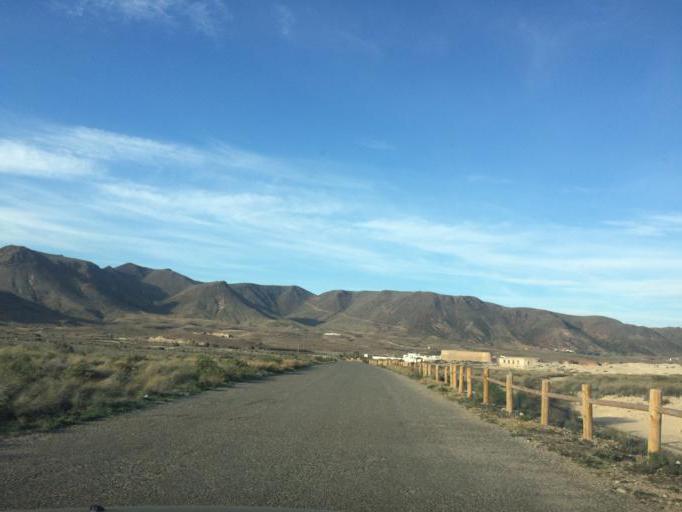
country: ES
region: Andalusia
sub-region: Provincia de Almeria
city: San Jose
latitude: 36.7978
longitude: -2.0634
